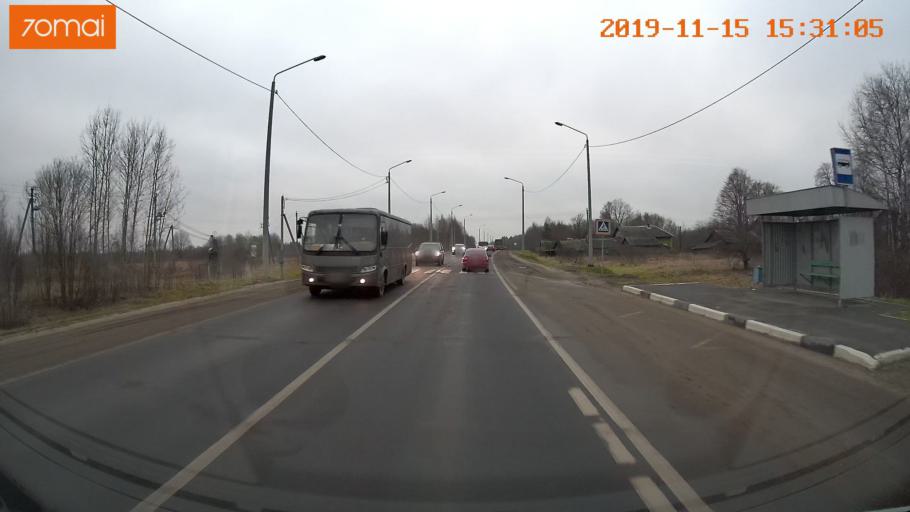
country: RU
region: Jaroslavl
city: Danilov
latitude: 58.1037
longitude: 40.1098
